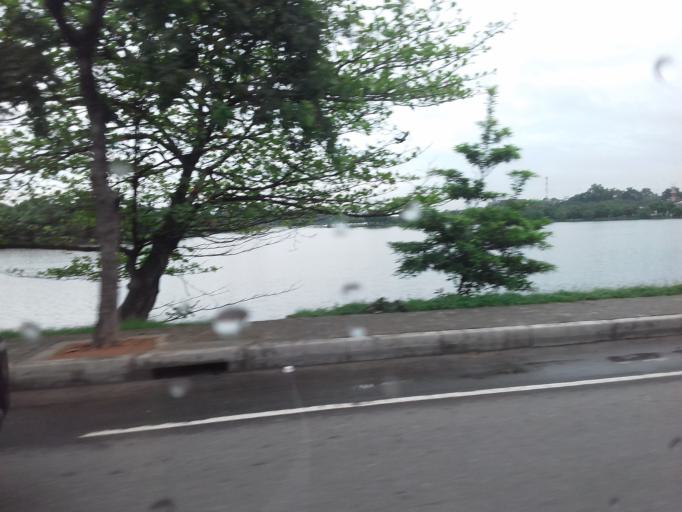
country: LK
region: Western
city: Battaramulla South
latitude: 6.9045
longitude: 79.9064
